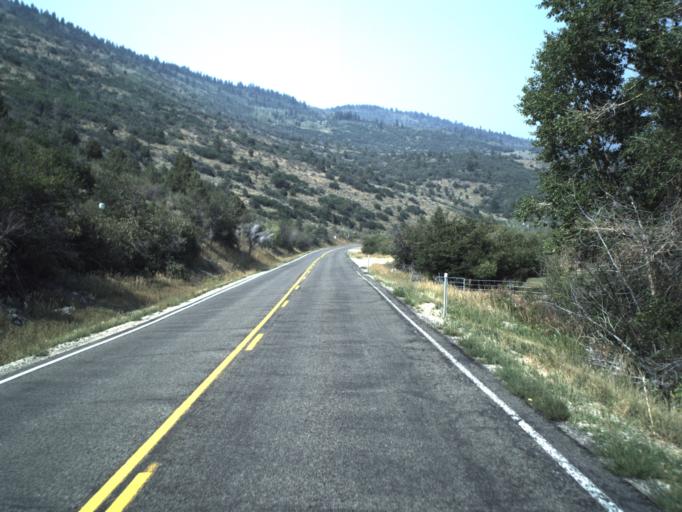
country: US
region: Utah
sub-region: Summit County
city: Francis
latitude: 40.6216
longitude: -111.2055
